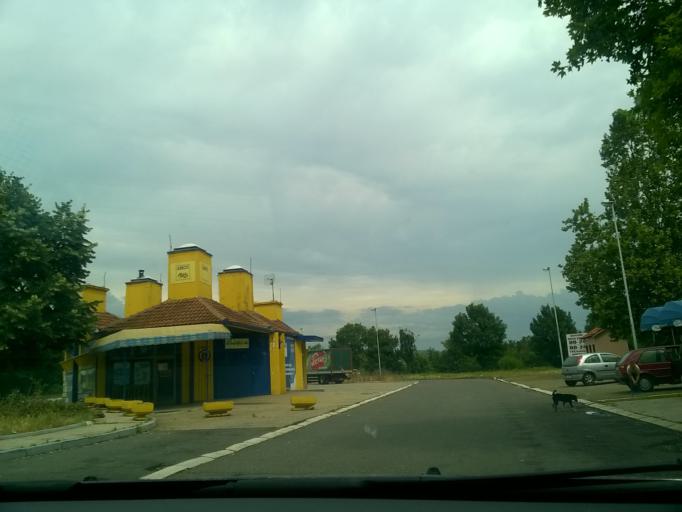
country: RS
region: Central Serbia
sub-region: Podunavski Okrug
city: Velika Plana
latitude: 44.3495
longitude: 21.0766
